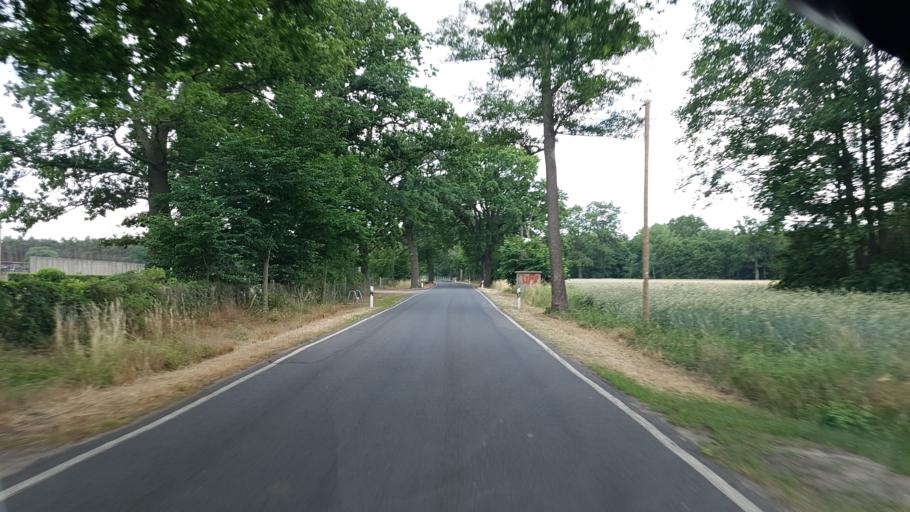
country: DE
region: Brandenburg
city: Kasel-Golzig
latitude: 51.9785
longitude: 13.6920
